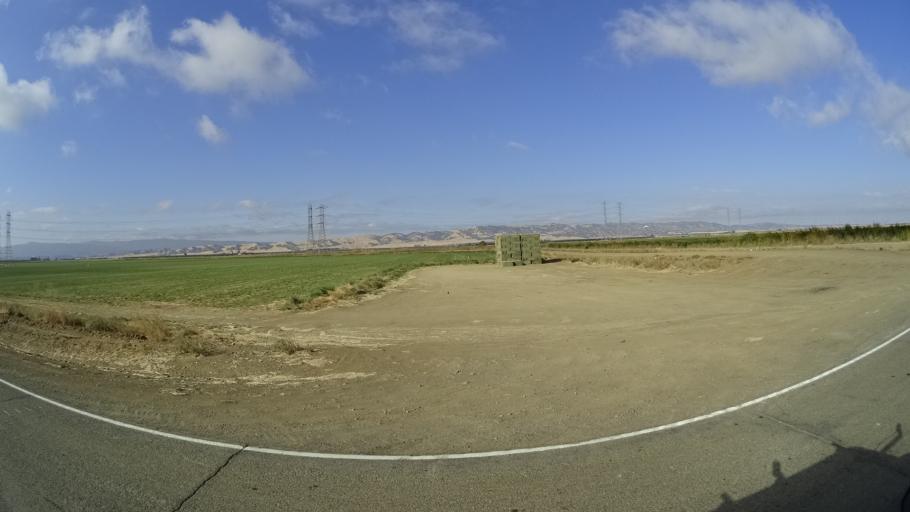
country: US
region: California
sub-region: Yolo County
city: Esparto
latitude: 38.7732
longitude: -122.0071
